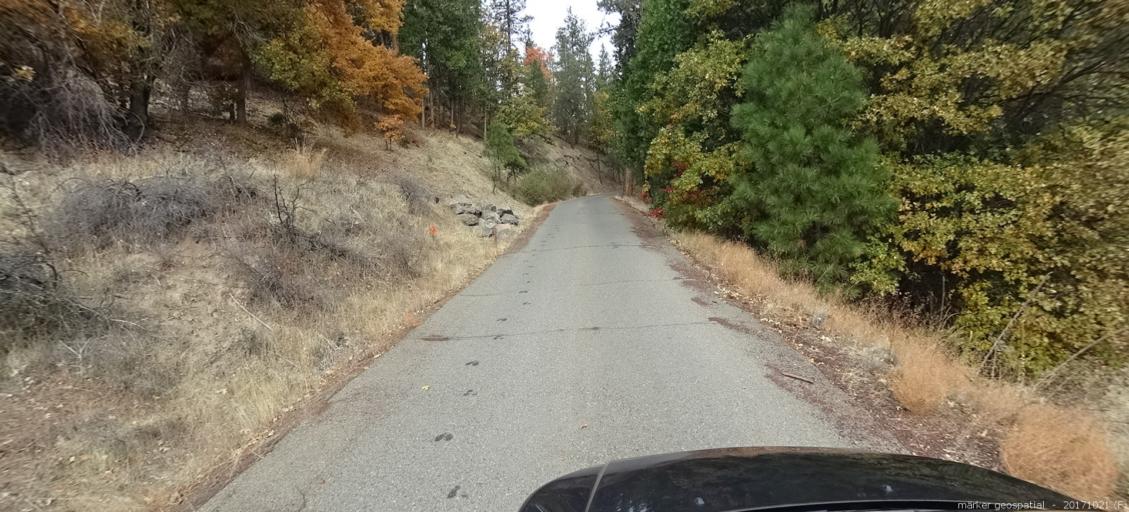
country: US
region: California
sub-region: Shasta County
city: Burney
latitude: 40.9617
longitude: -121.5487
